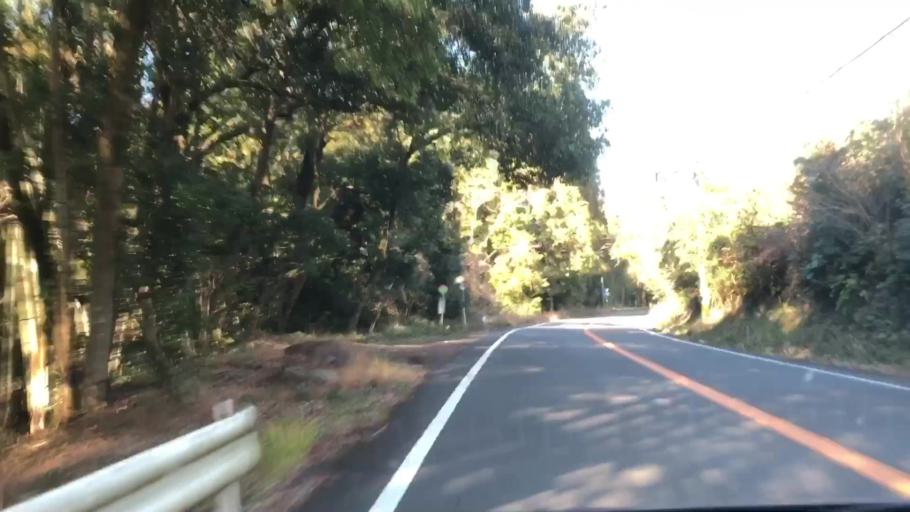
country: JP
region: Kagoshima
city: Satsumasendai
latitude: 31.8550
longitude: 130.4293
